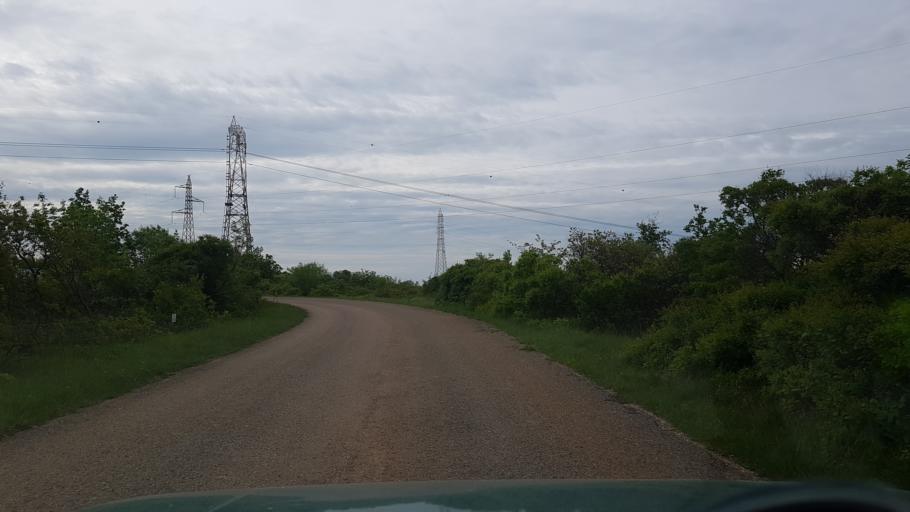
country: IT
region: Friuli Venezia Giulia
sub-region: Provincia di Gorizia
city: Ronchi dei Legionari
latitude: 45.8474
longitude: 13.5036
